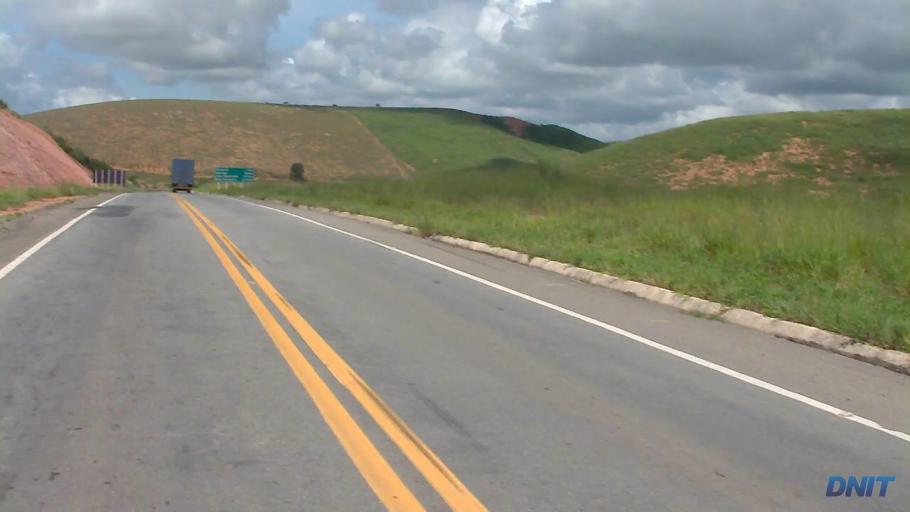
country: BR
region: Minas Gerais
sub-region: Belo Oriente
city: Belo Oriente
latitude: -19.1061
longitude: -42.2021
